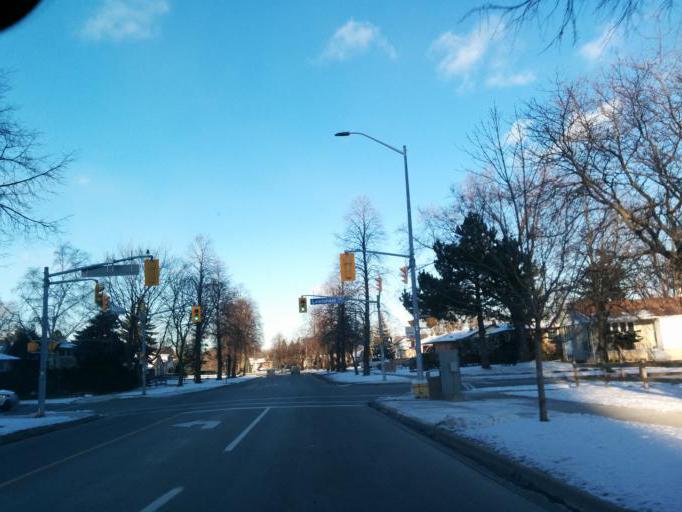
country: CA
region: Ontario
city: Mississauga
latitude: 43.5149
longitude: -79.6442
